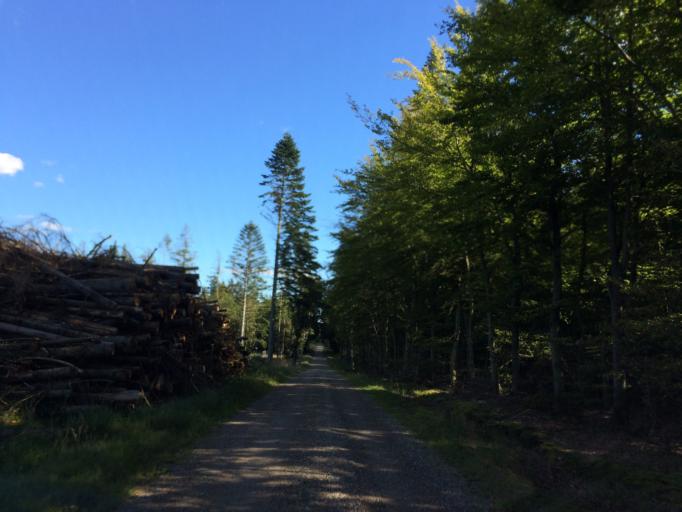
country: DK
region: Central Jutland
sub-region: Holstebro Kommune
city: Ulfborg
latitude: 56.2627
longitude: 8.4381
